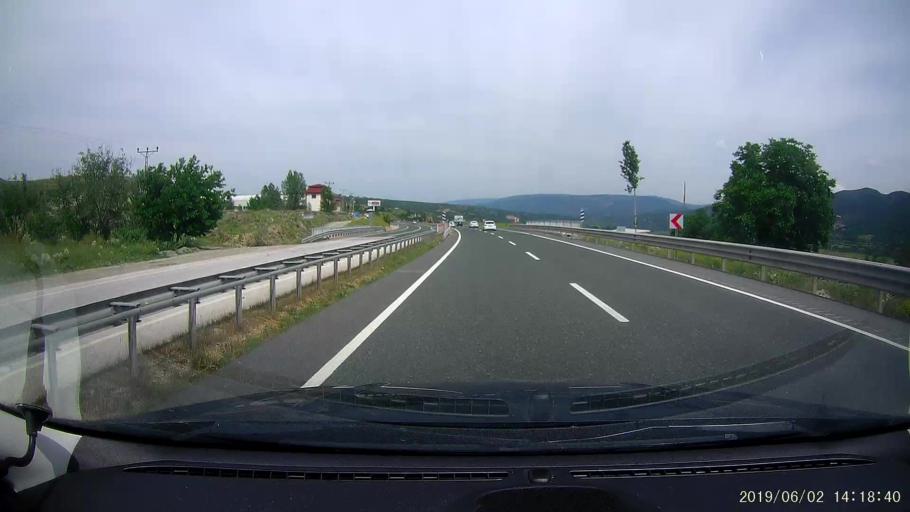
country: TR
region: Kastamonu
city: Tosya
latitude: 40.9564
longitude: 33.9609
